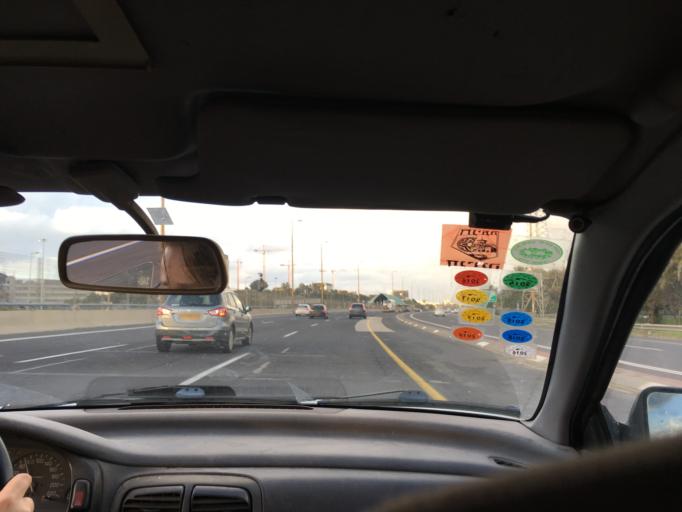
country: IL
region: Tel Aviv
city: Ramat Gan
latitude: 32.1004
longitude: 34.8031
